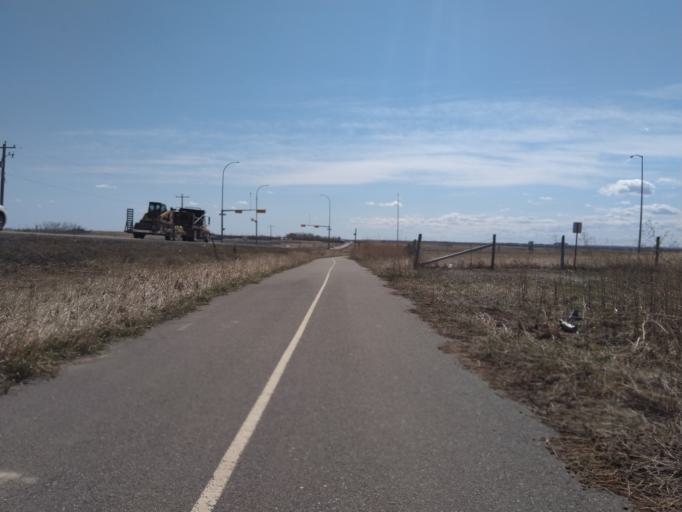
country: CA
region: Alberta
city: Chestermere
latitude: 50.9486
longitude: -113.9121
